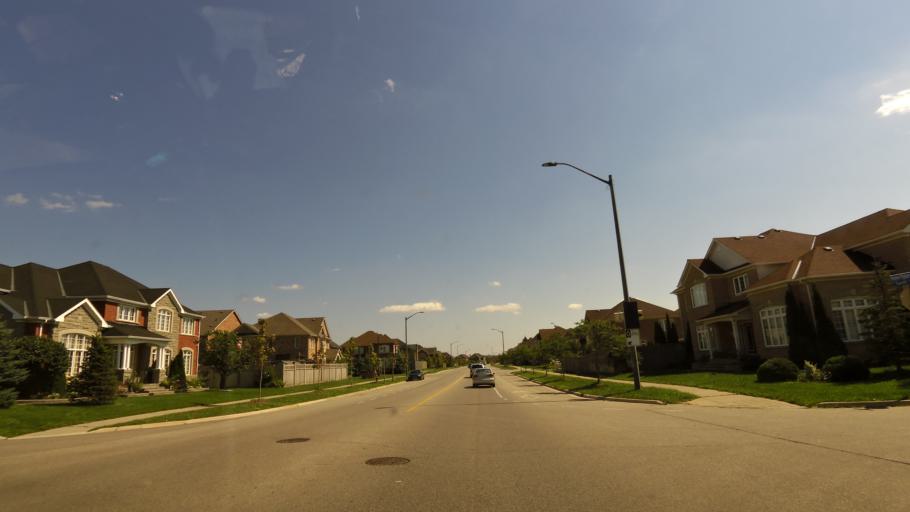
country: CA
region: Ontario
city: Mississauga
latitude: 43.5518
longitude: -79.7322
